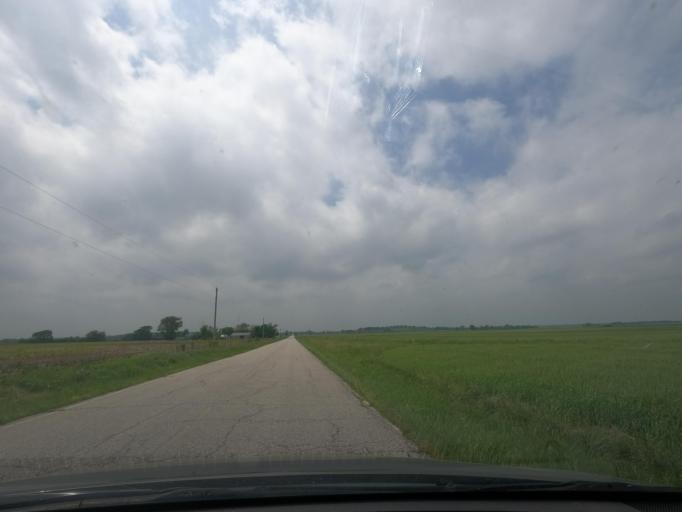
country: US
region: Kansas
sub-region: Cherokee County
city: Columbus
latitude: 37.2818
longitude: -94.9418
